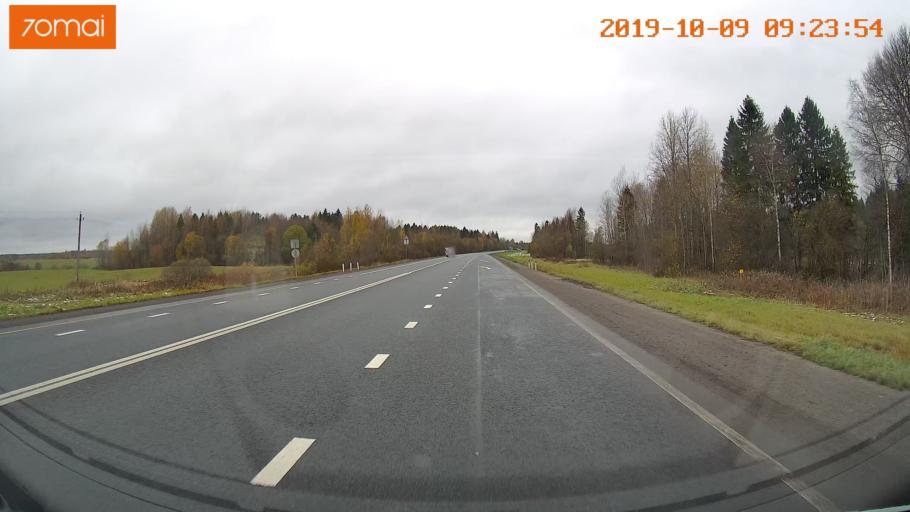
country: RU
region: Vologda
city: Vologda
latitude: 59.0739
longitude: 40.0244
